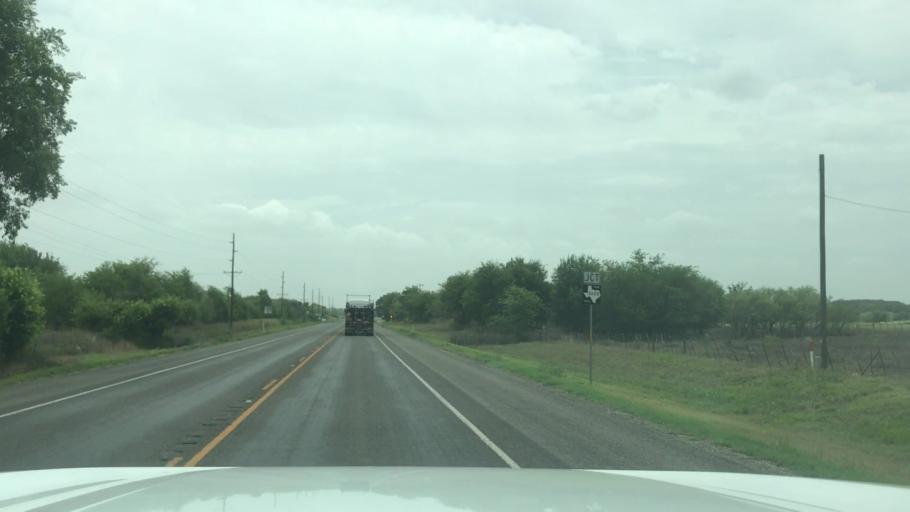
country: US
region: Texas
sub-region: Bosque County
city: Clifton
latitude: 31.7363
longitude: -97.5515
